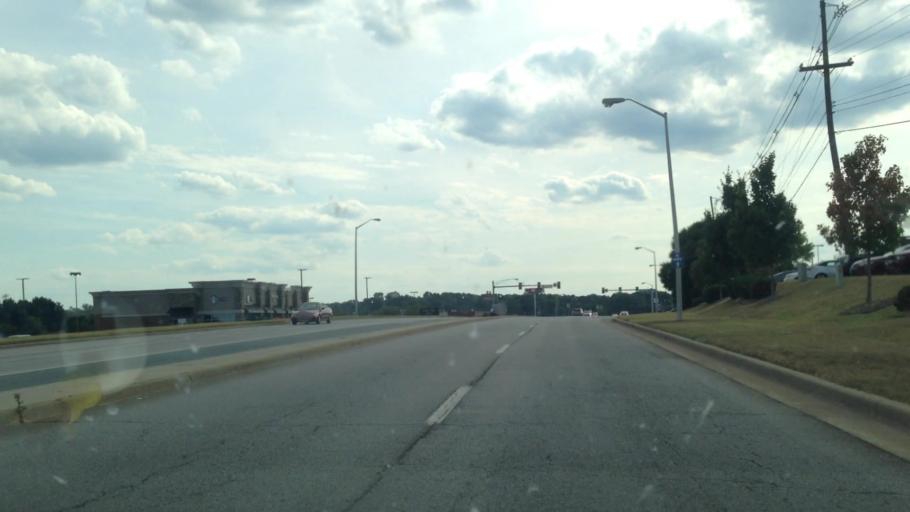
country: US
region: Virginia
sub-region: City of Danville
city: Danville
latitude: 36.5957
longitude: -79.4231
